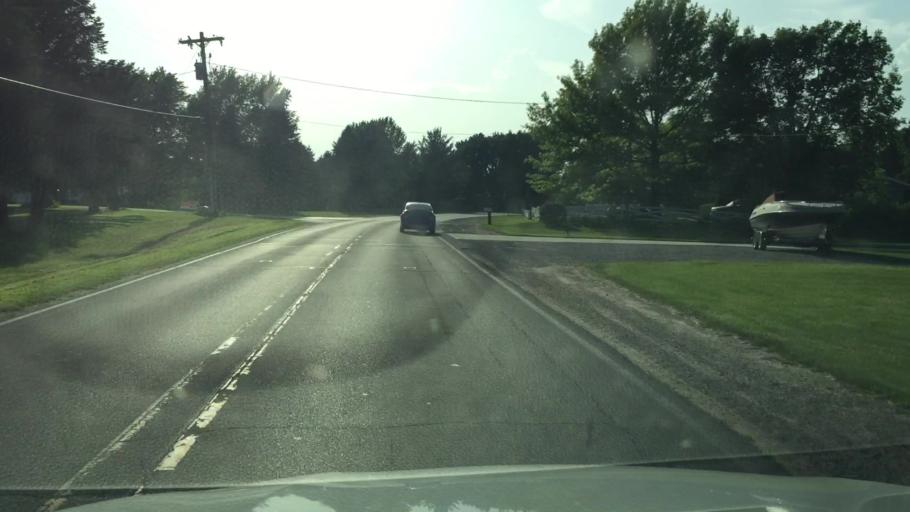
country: US
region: Iowa
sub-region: Linn County
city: Ely
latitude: 41.8409
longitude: -91.6431
